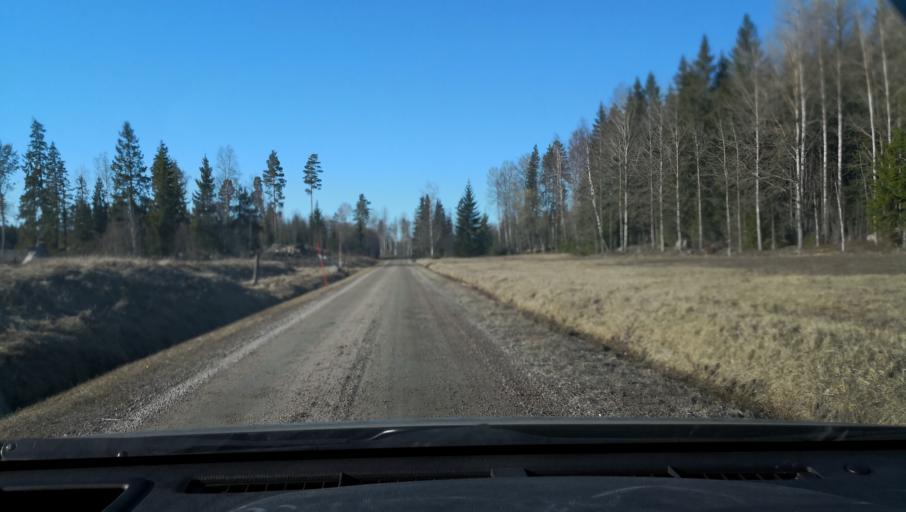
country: SE
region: Dalarna
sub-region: Avesta Kommun
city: Horndal
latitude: 60.1746
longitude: 16.6321
